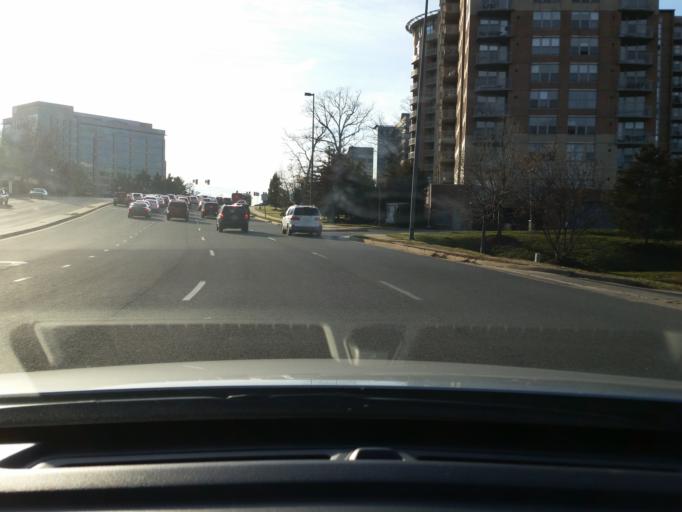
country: US
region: Virginia
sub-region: Fairfax County
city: Reston
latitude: 38.9552
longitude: -77.3529
